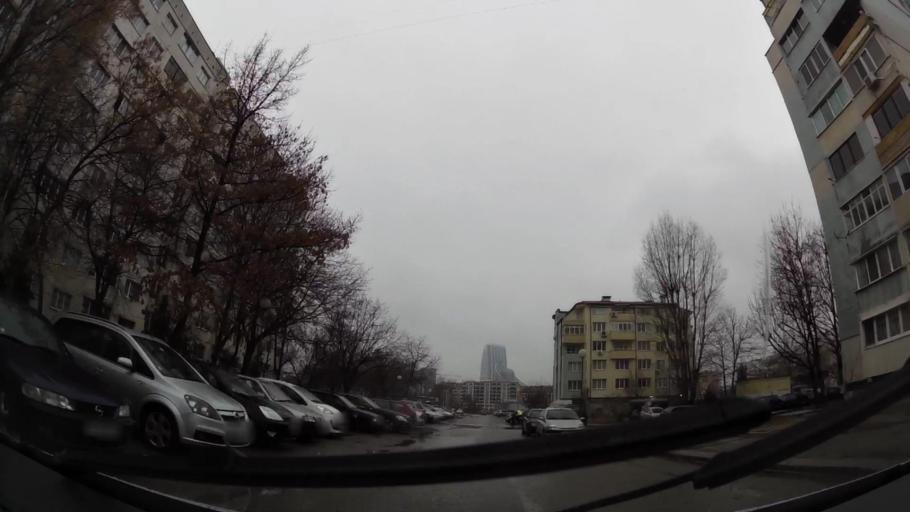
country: BG
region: Sofia-Capital
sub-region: Stolichna Obshtina
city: Sofia
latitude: 42.6463
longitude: 23.4071
